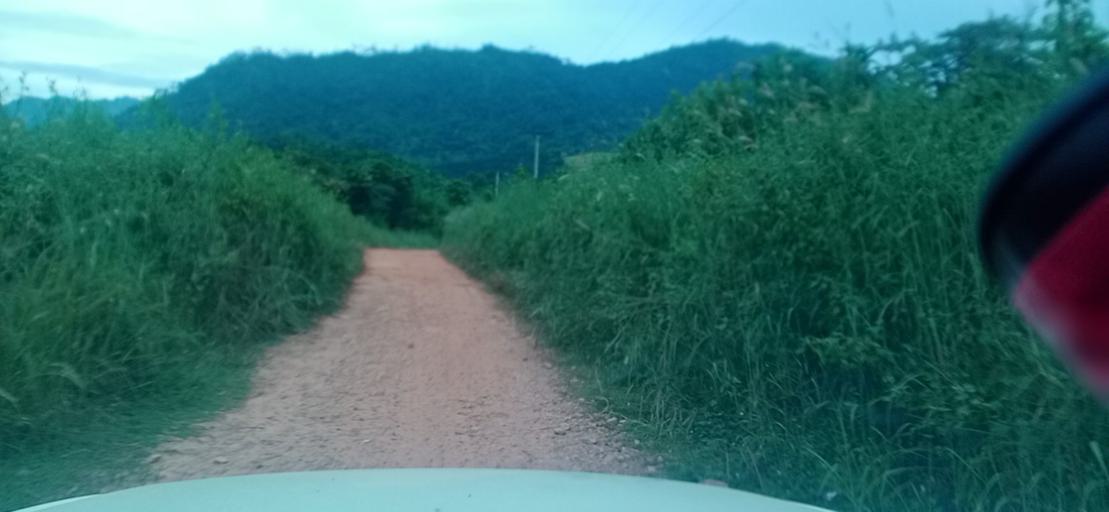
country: TH
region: Changwat Bueng Kan
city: Pak Khat
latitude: 18.5657
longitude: 103.3070
